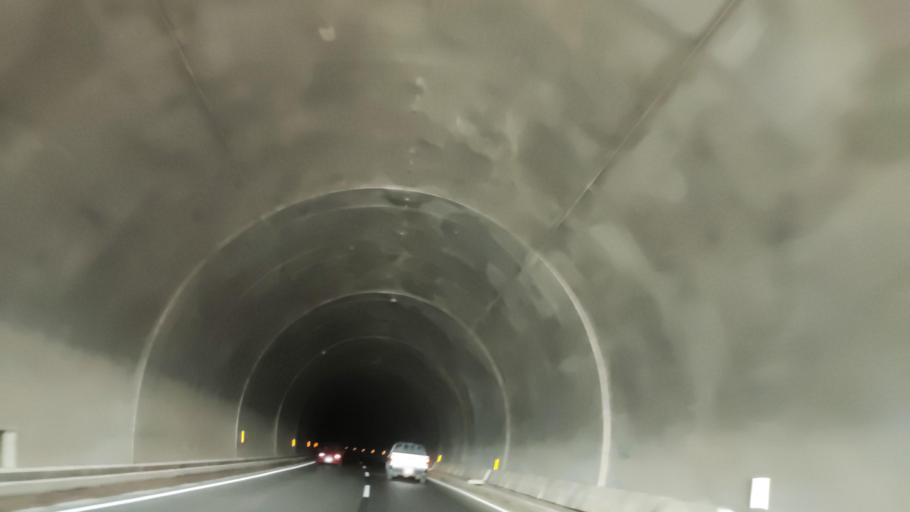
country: IQ
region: Arbil
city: Shaqlawah
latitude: 36.4396
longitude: 44.2837
